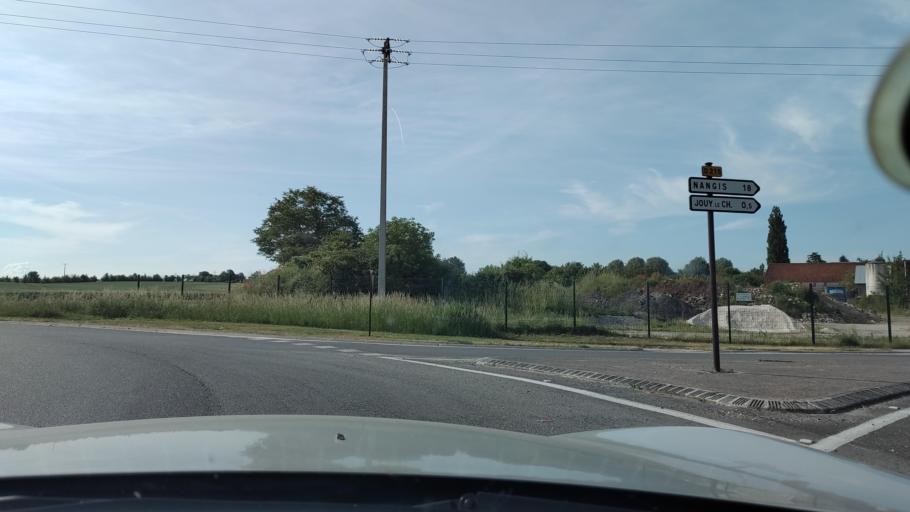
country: FR
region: Ile-de-France
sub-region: Departement de Seine-et-Marne
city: Jouy-le-Chatel
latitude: 48.6690
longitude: 3.1316
